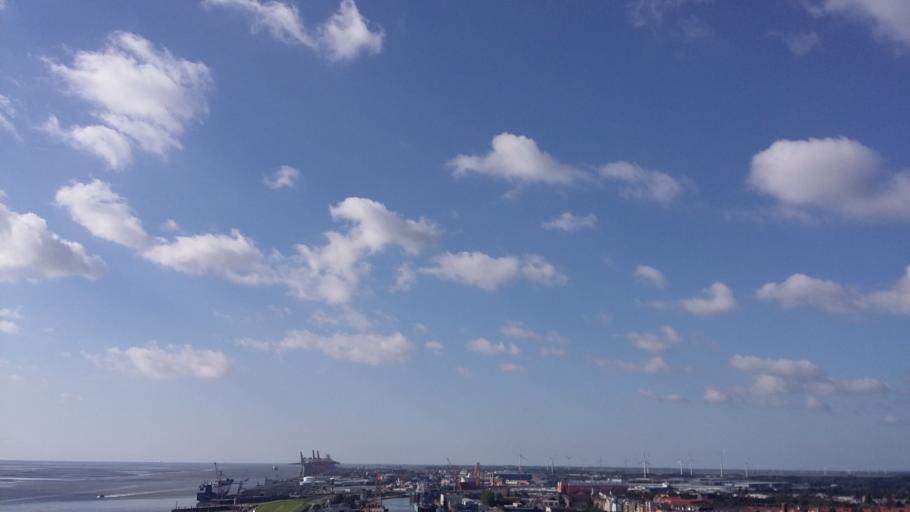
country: DE
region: Bremen
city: Bremerhaven
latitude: 53.5428
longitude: 8.5739
